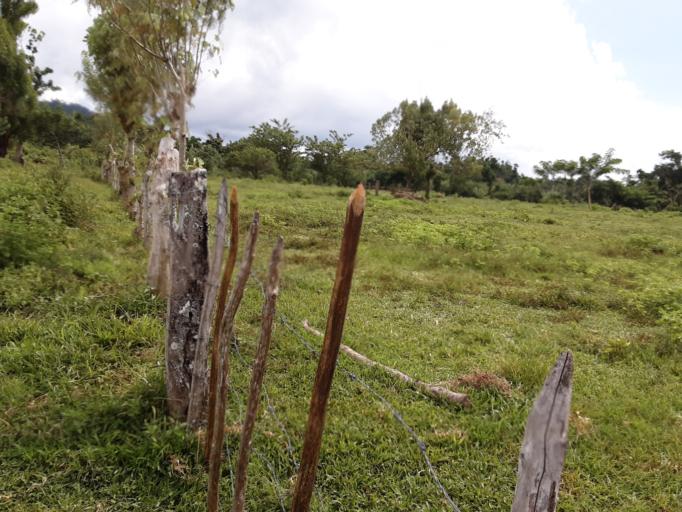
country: VU
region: Sanma
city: Luganville
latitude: -15.5795
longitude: 167.0054
